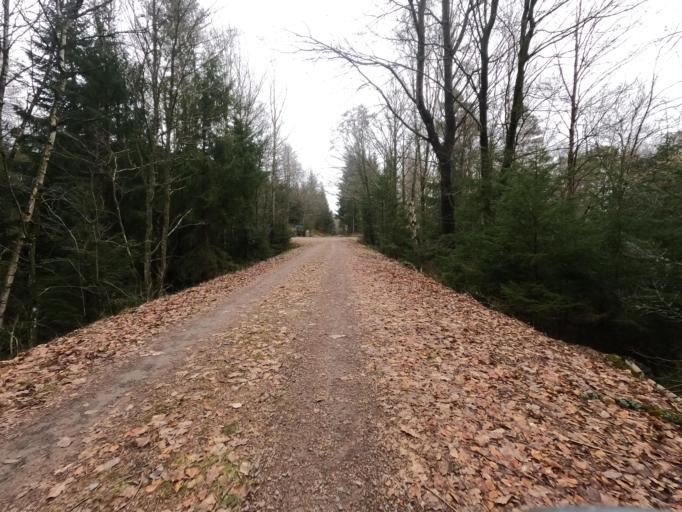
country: SE
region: Kronoberg
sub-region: Markaryds Kommun
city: Stromsnasbruk
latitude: 56.7908
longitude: 13.6274
